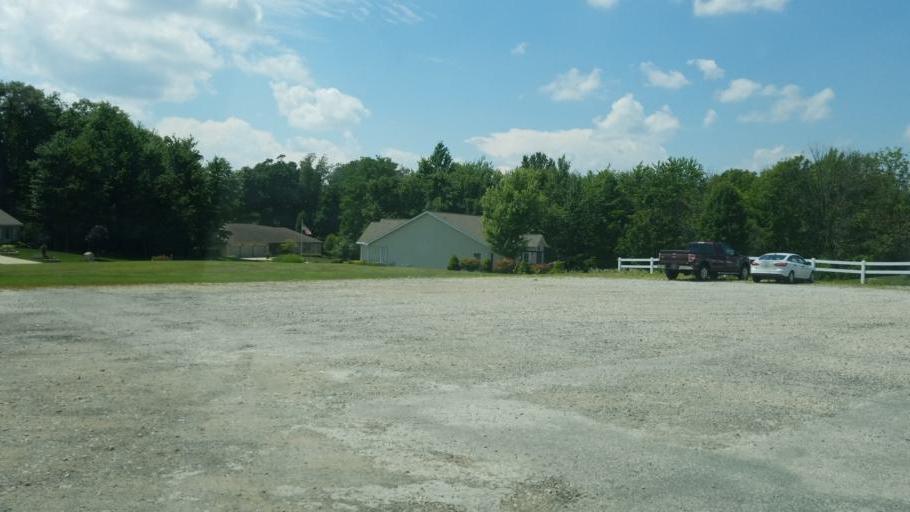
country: US
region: Ohio
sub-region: Richland County
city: Ontario
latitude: 40.7925
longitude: -82.6057
